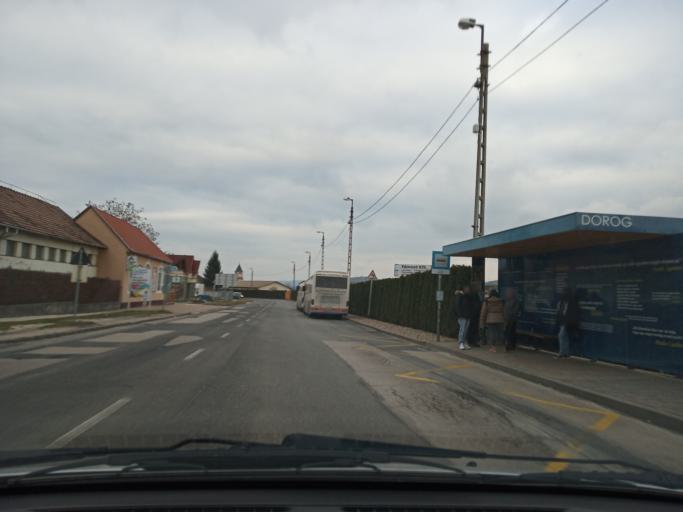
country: HU
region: Komarom-Esztergom
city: Dorog
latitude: 47.7220
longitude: 18.7295
